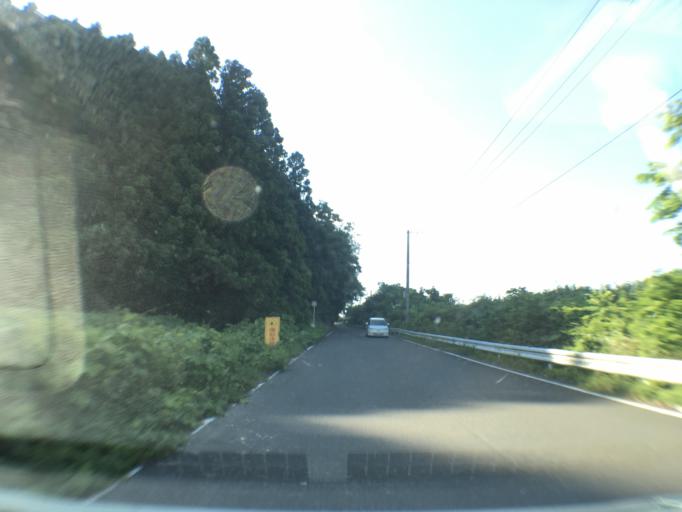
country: JP
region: Miyagi
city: Wakuya
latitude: 38.6253
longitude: 141.2902
